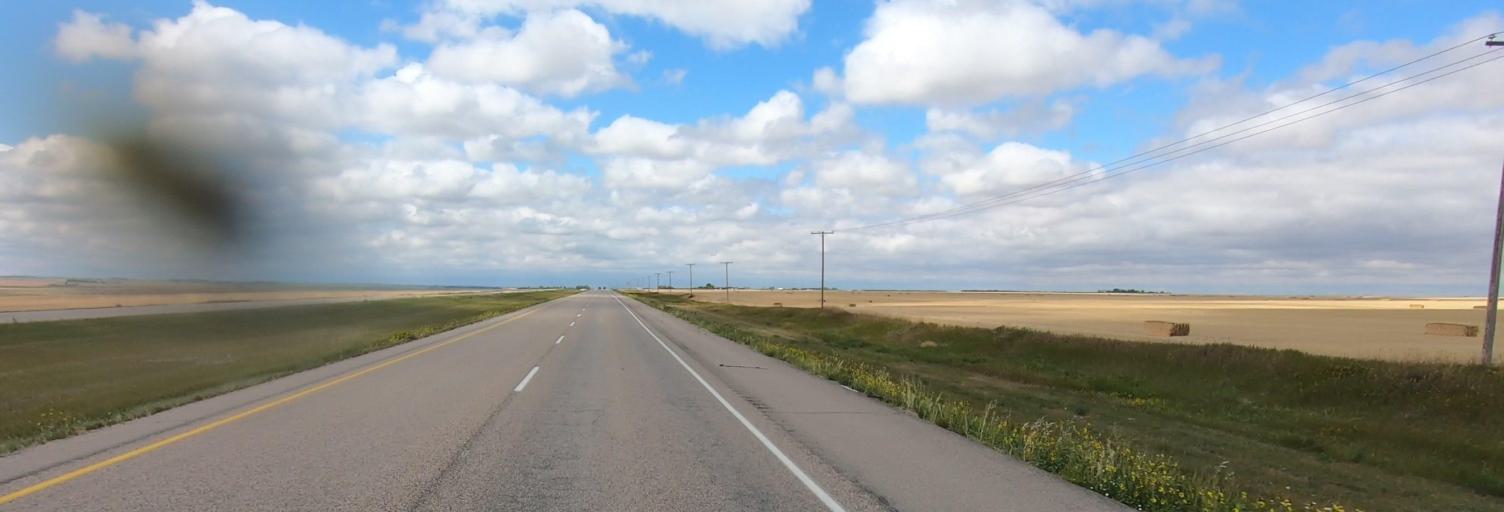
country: CA
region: Saskatchewan
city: Moose Jaw
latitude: 50.4287
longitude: -105.7382
